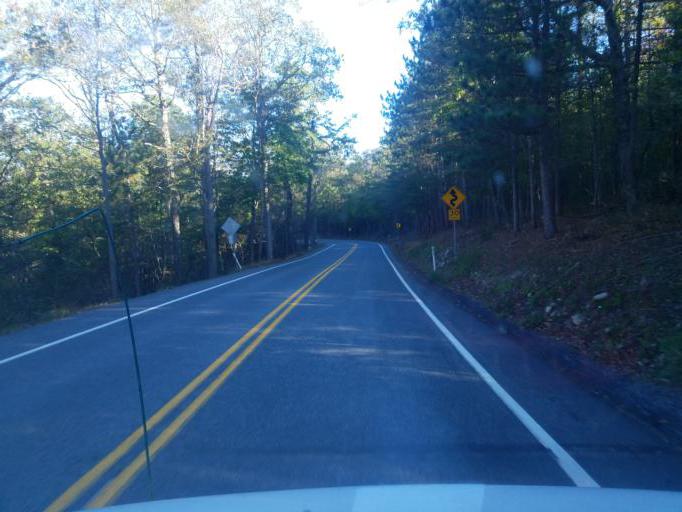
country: US
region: Pennsylvania
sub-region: Franklin County
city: Mont Alto
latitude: 39.8442
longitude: -77.5172
